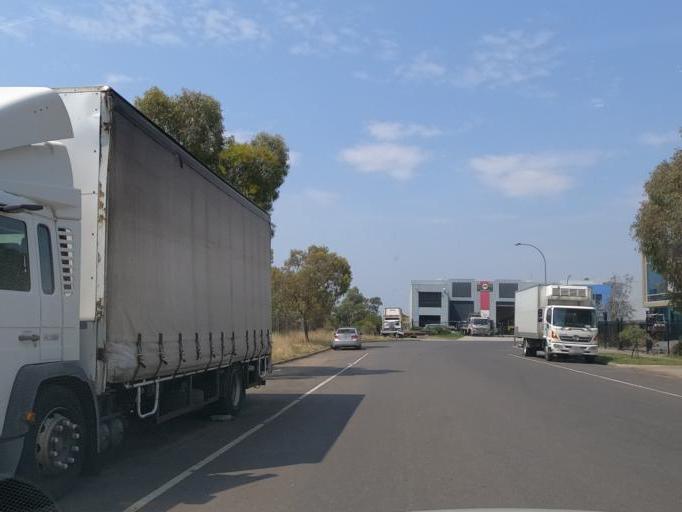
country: AU
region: Victoria
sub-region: Hume
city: Craigieburn
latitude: -37.6179
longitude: 144.9450
